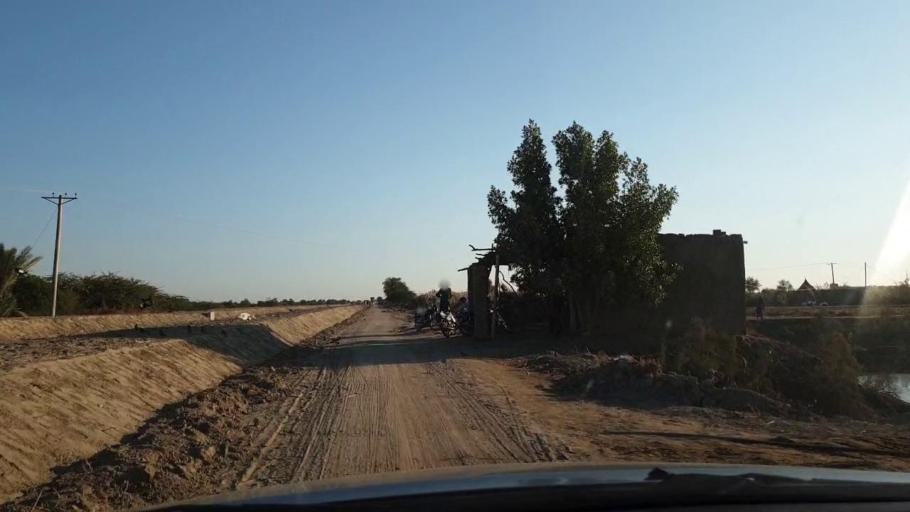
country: PK
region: Sindh
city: Tando Mittha Khan
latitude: 25.8397
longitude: 69.1730
